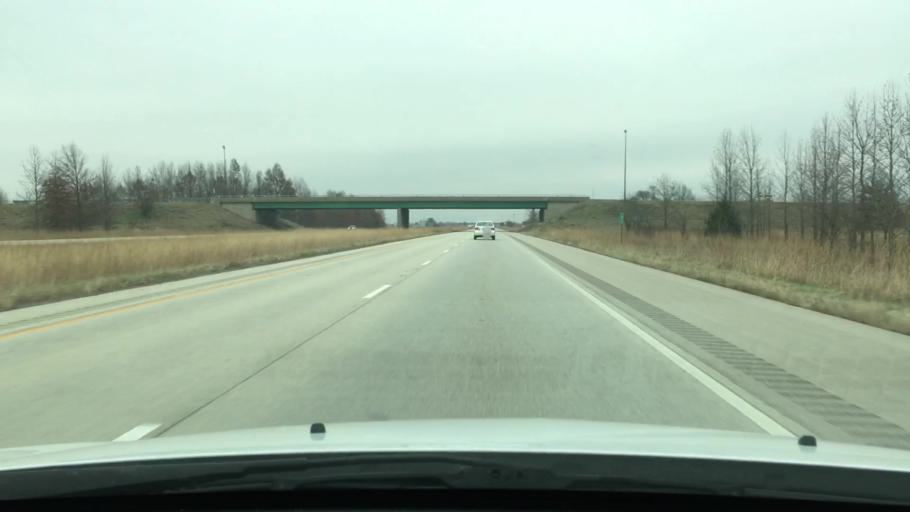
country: US
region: Illinois
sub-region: Sangamon County
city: New Berlin
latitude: 39.7400
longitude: -89.9261
